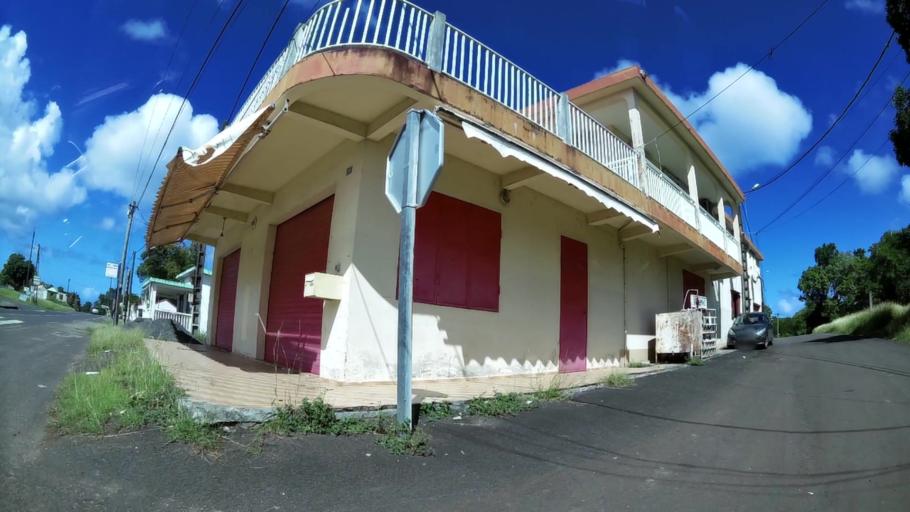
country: GP
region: Guadeloupe
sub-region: Guadeloupe
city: Anse-Bertrand
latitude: 16.4703
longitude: -61.5006
